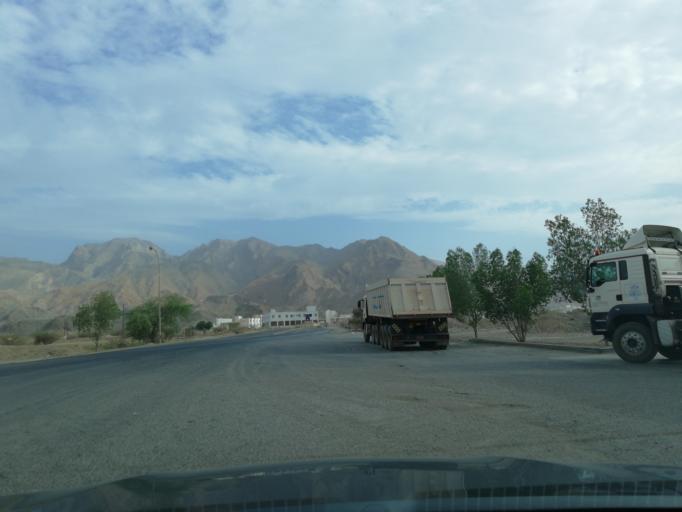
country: OM
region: Muhafazat Masqat
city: Bawshar
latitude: 23.4820
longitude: 58.2871
